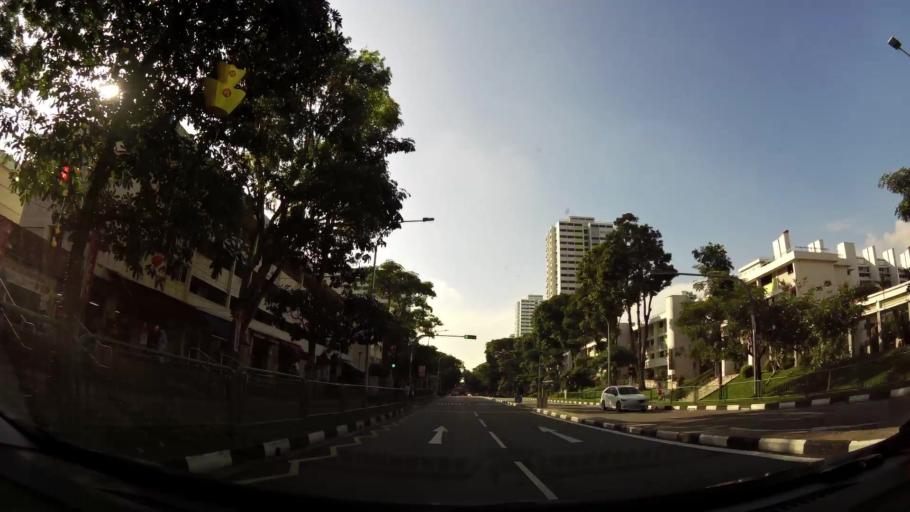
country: SG
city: Singapore
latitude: 1.3327
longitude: 103.9302
